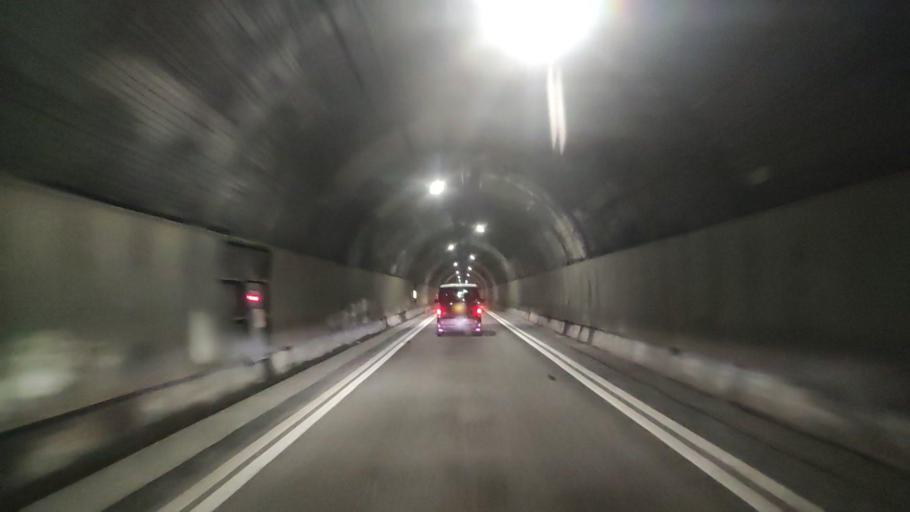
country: JP
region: Fukui
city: Takefu
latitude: 35.8434
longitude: 136.1239
